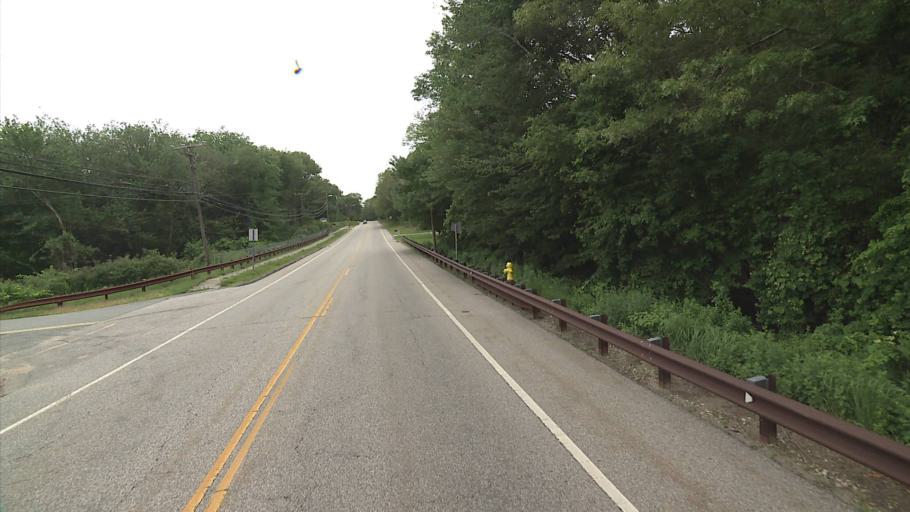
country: US
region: Connecticut
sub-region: New London County
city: Poquonock Bridge
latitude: 41.3771
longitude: -72.0266
